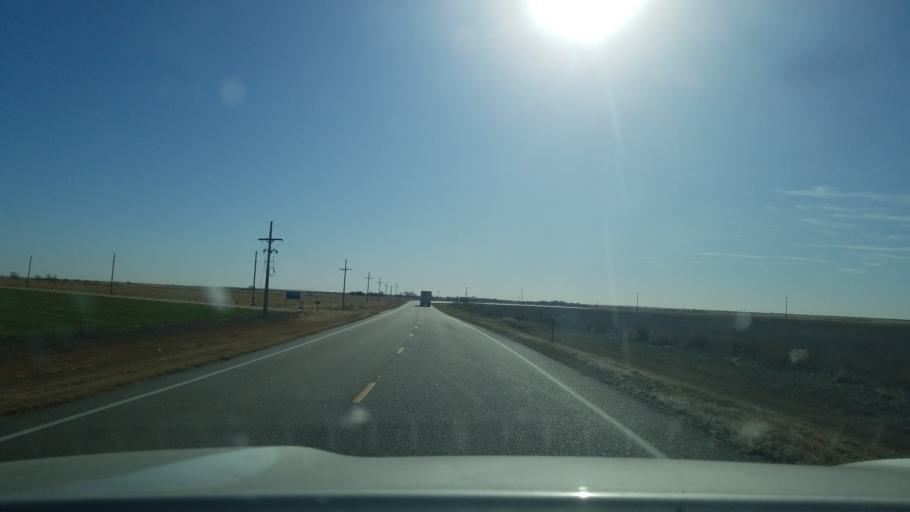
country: US
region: Kansas
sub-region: Ness County
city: Ness City
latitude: 38.4313
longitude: -99.9032
